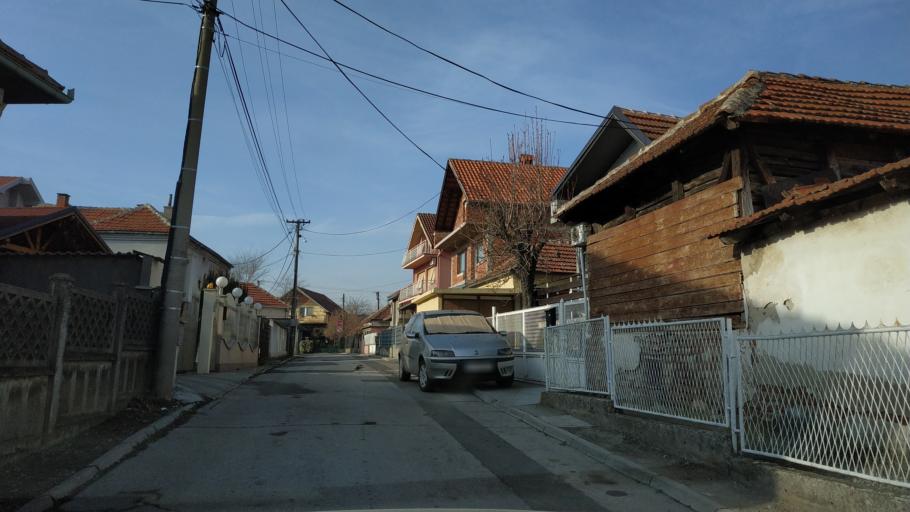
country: RS
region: Central Serbia
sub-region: Nisavski Okrug
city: Aleksinac
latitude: 43.5380
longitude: 21.7022
